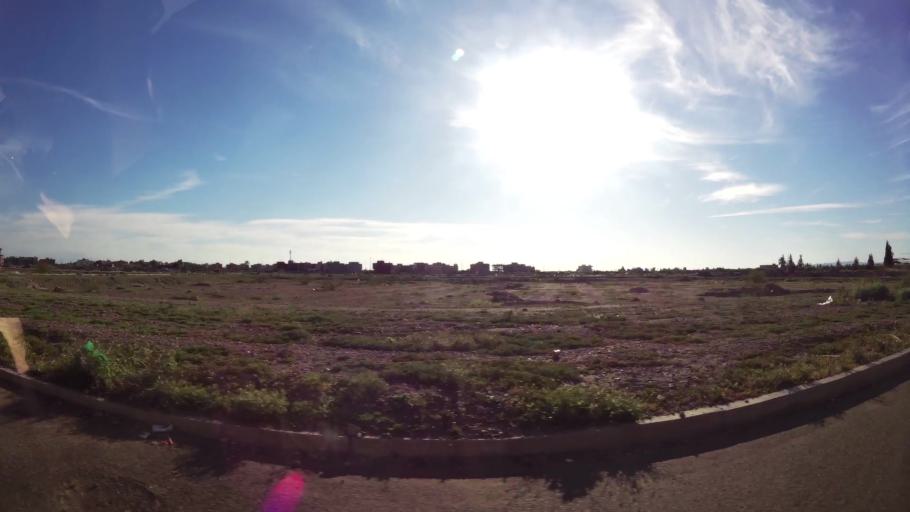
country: MA
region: Marrakech-Tensift-Al Haouz
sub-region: Marrakech
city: Marrakesh
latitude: 31.6772
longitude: -8.0678
